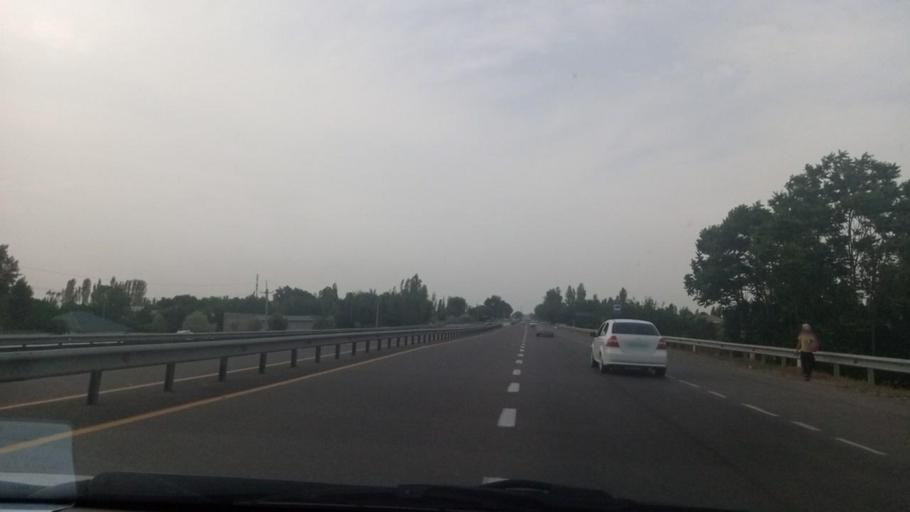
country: UZ
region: Toshkent Shahri
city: Bektemir
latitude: 41.1499
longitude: 69.4280
